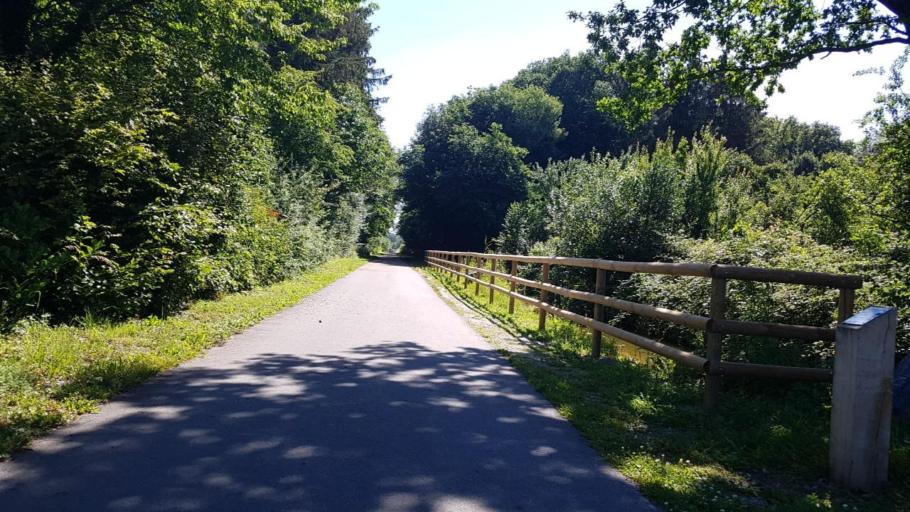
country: BE
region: Wallonia
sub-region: Province du Hainaut
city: Momignies
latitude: 50.0269
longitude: 4.1765
